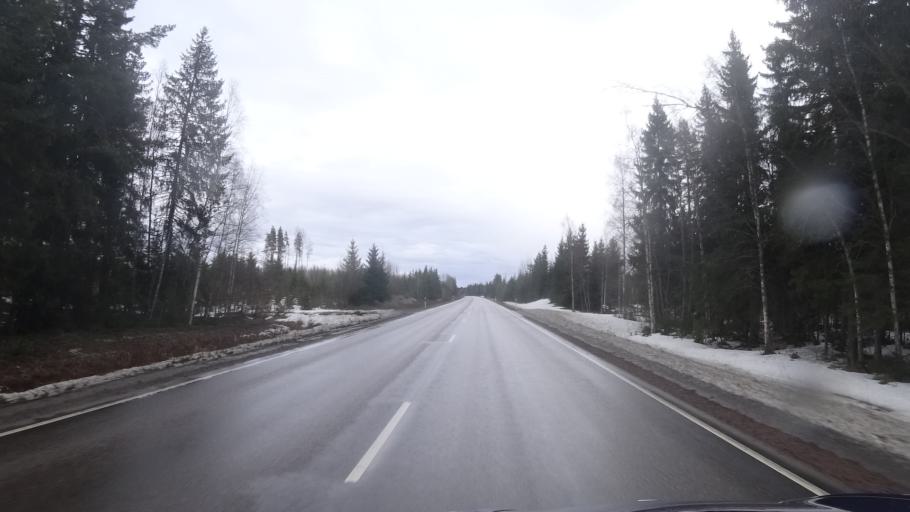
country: FI
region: Kymenlaakso
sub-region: Kouvola
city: Elimaeki
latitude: 60.6901
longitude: 26.5814
